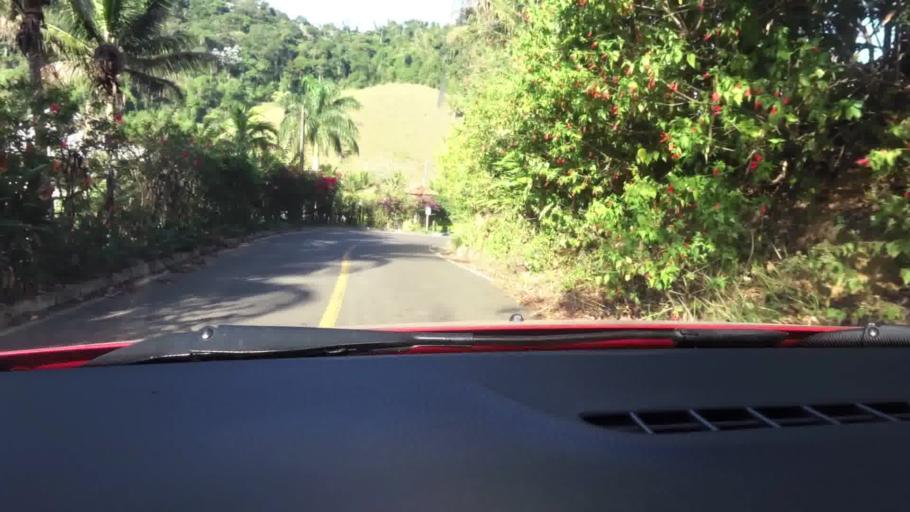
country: BR
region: Espirito Santo
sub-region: Guarapari
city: Guarapari
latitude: -20.5682
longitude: -40.5470
